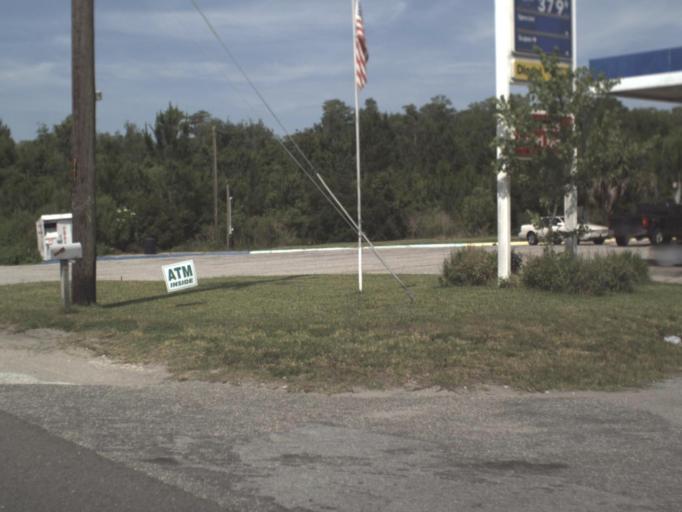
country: US
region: Florida
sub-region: Saint Johns County
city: Saint Augustine South
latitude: 29.8235
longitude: -81.3810
